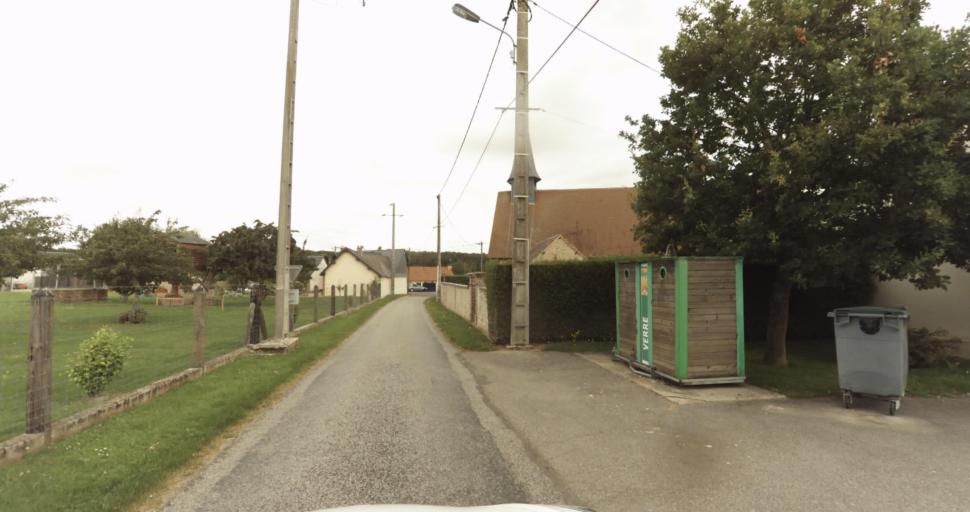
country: FR
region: Haute-Normandie
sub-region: Departement de l'Eure
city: Tillieres-sur-Avre
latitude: 48.7956
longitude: 1.0988
